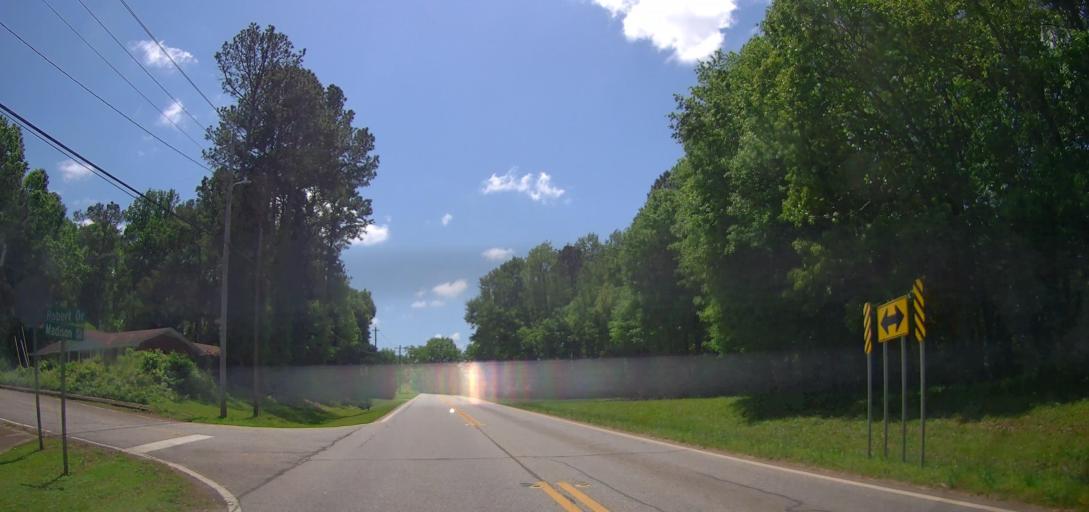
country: US
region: Georgia
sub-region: Jasper County
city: Monticello
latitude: 33.3122
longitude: -83.6764
